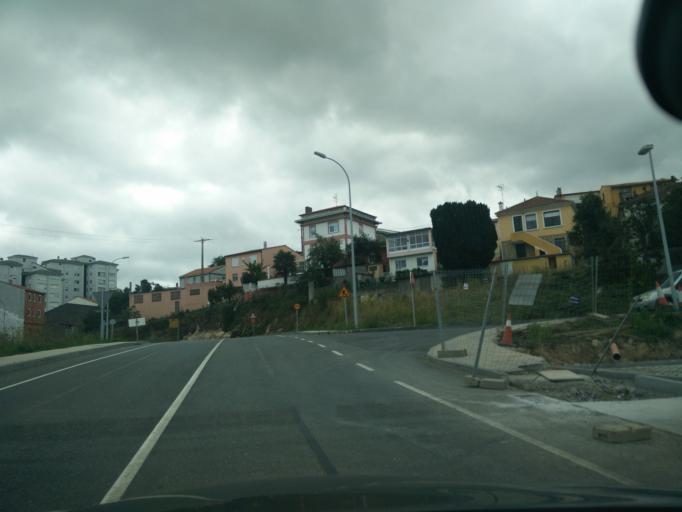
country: ES
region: Galicia
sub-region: Provincia da Coruna
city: A Coruna
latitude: 43.3437
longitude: -8.4158
